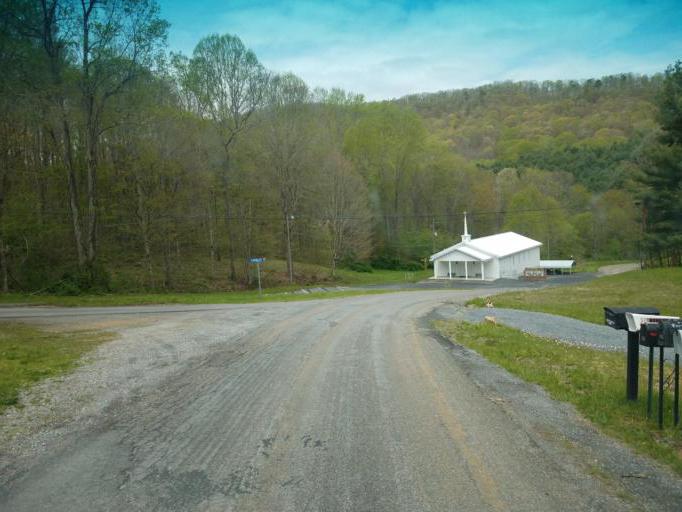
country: US
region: Virginia
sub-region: Smyth County
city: Marion
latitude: 36.8055
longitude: -81.4653
